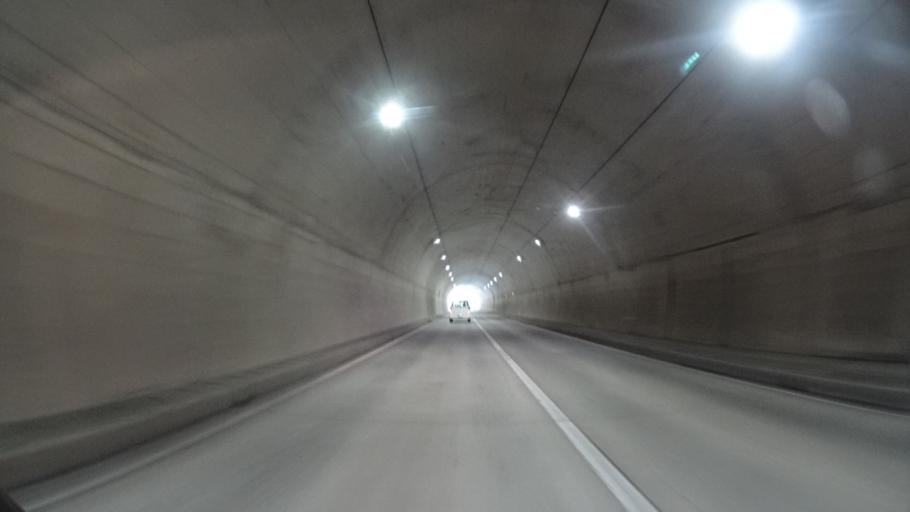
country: JP
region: Ehime
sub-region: Nishiuwa-gun
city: Ikata-cho
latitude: 33.4323
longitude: 132.2159
